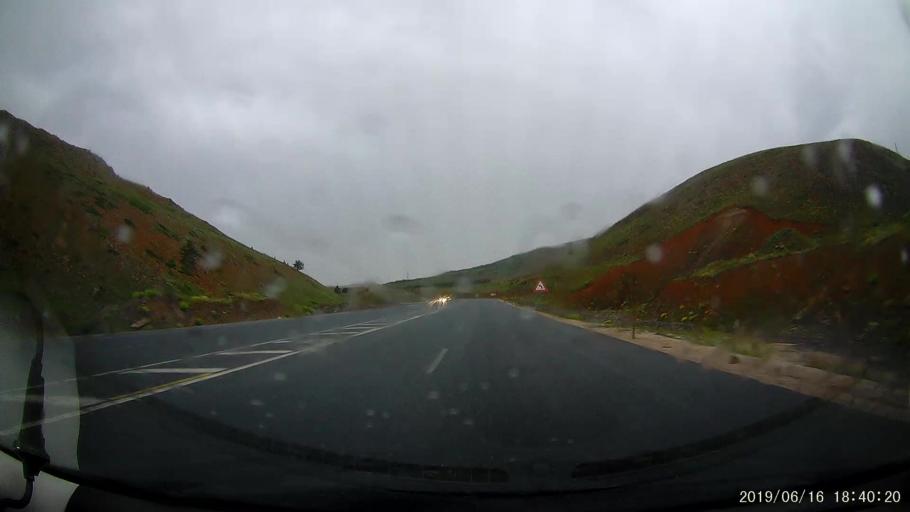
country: TR
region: Erzincan
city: Catalarmut
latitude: 39.8808
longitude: 39.1490
